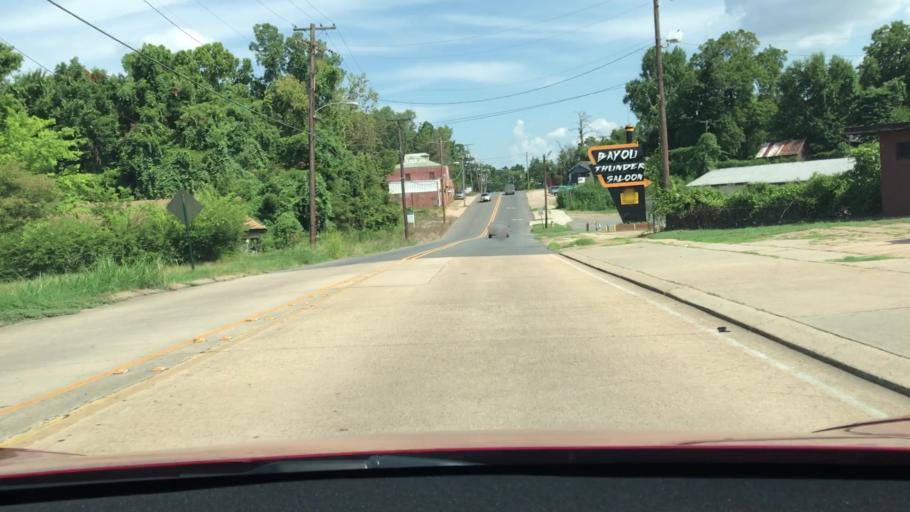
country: US
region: Louisiana
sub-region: Bossier Parish
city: Bossier City
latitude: 32.5032
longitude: -93.7363
